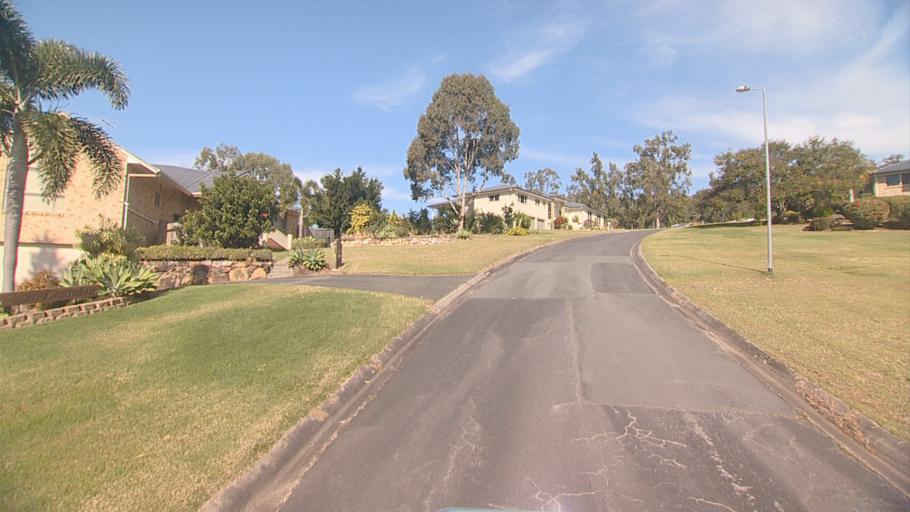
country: AU
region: Queensland
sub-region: Logan
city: Windaroo
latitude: -27.7607
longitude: 153.1798
